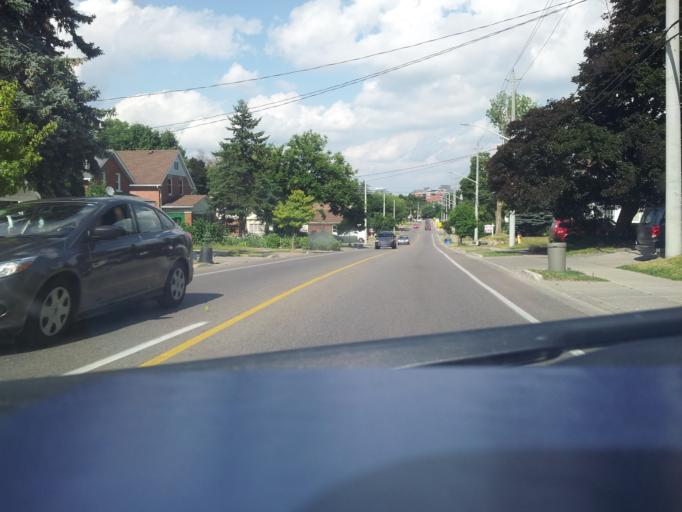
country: CA
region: Ontario
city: Kitchener
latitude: 43.4435
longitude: -80.5108
